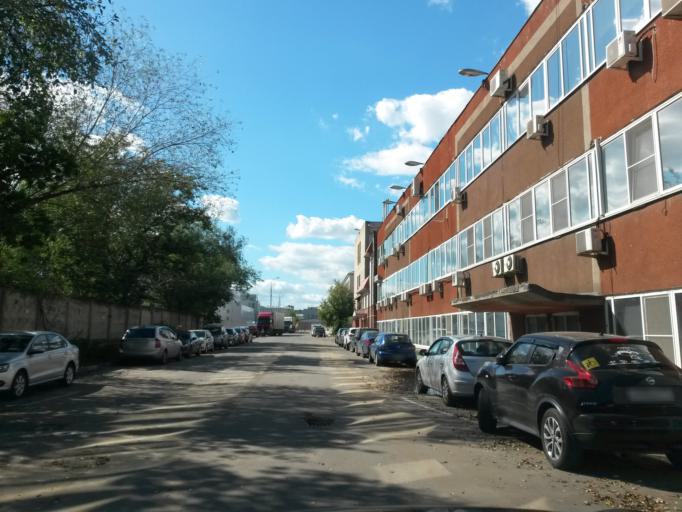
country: RU
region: Moskovskaya
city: Kozhukhovo
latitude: 55.7029
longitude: 37.6990
